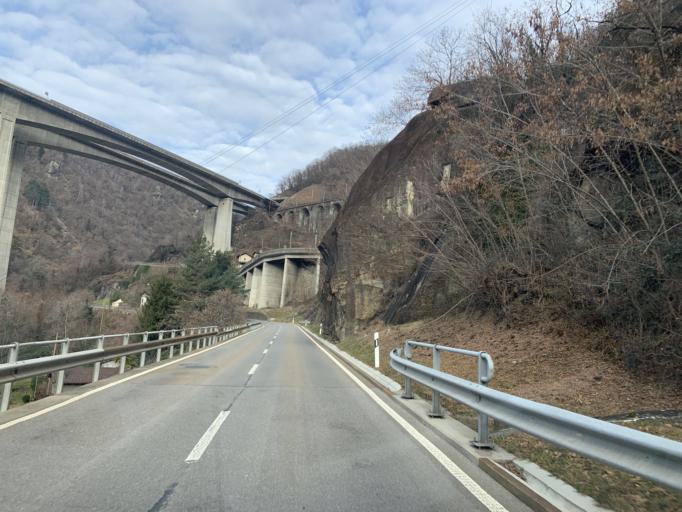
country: CH
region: Ticino
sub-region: Blenio District
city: Cancori
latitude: 46.4206
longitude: 8.8606
